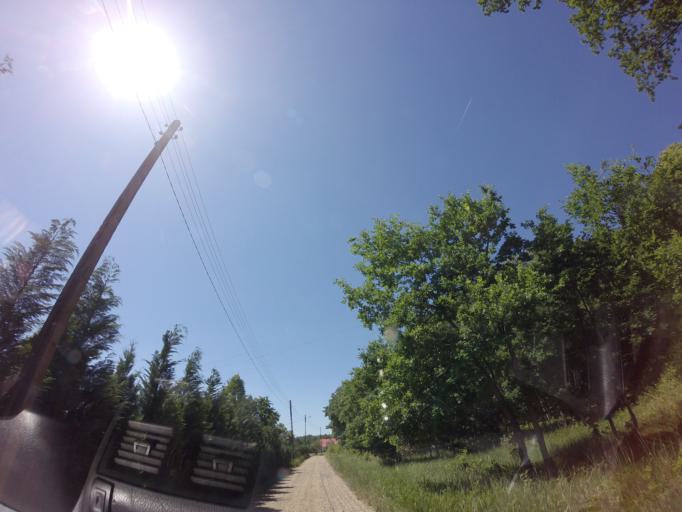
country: PL
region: Lubusz
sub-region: Powiat strzelecko-drezdenecki
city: Dobiegniew
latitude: 53.0742
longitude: 15.8514
